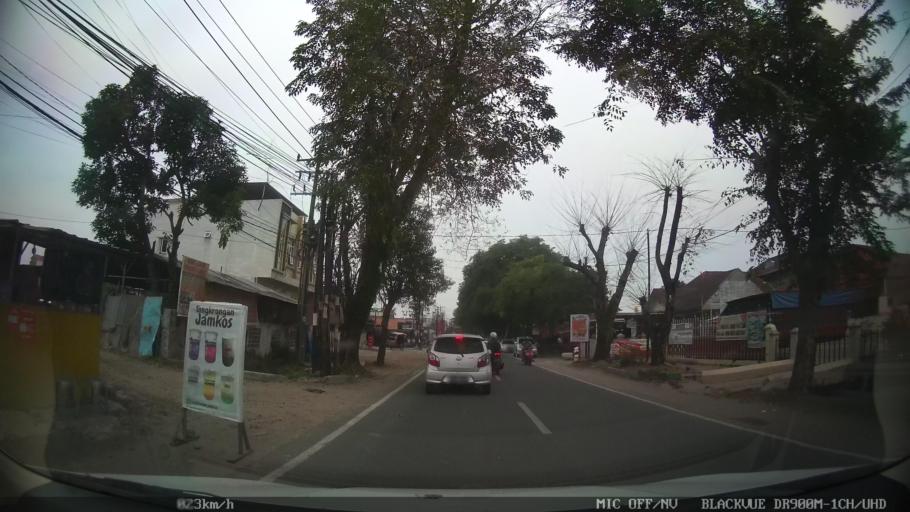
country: ID
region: North Sumatra
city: Medan
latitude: 3.5684
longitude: 98.7074
